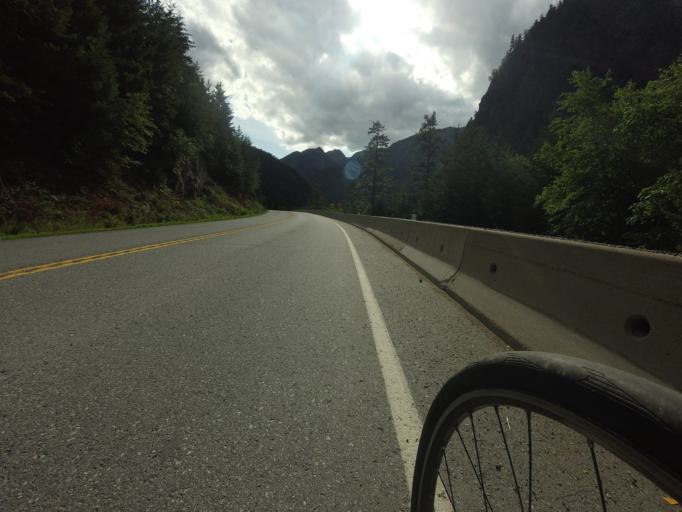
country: CA
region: British Columbia
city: Lillooet
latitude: 50.6411
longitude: -122.0709
